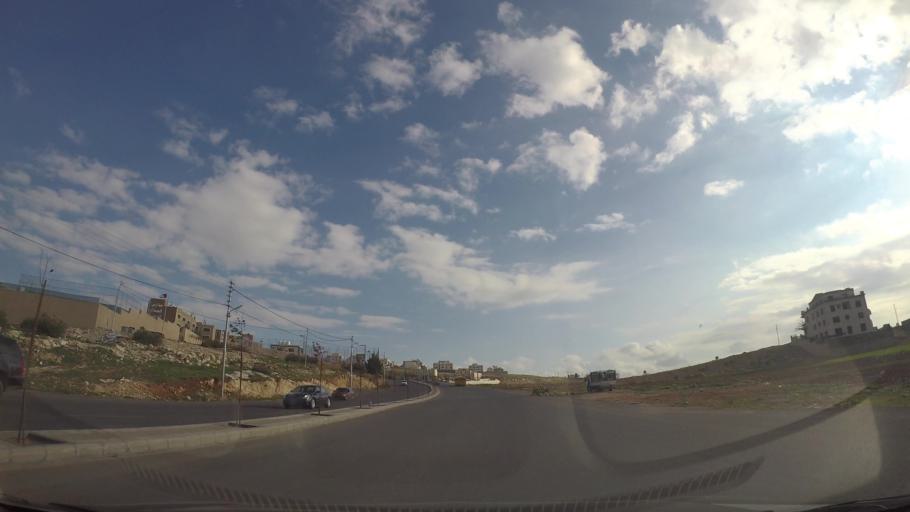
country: JO
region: Amman
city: Wadi as Sir
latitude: 31.9308
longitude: 35.8479
